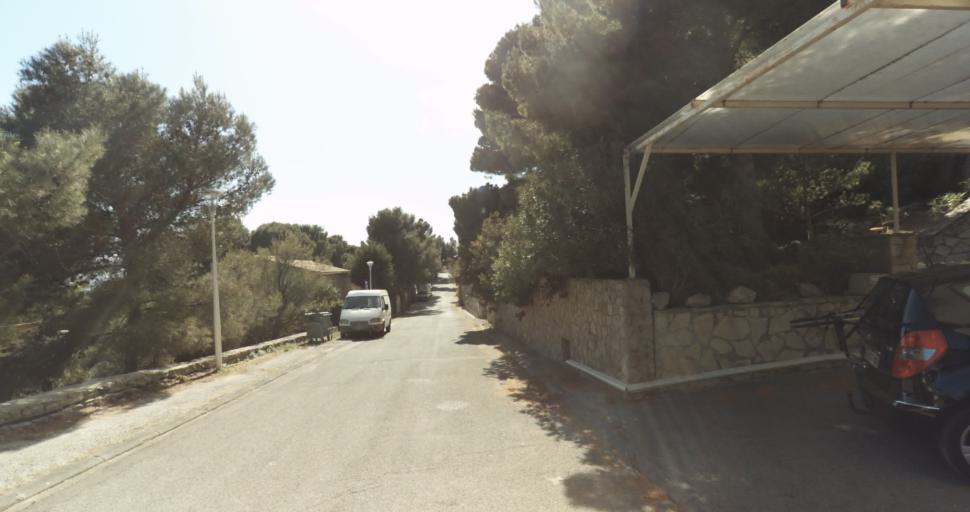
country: FR
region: Languedoc-Roussillon
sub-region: Departement de l'Aude
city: Leucate
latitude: 42.9060
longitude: 3.0523
